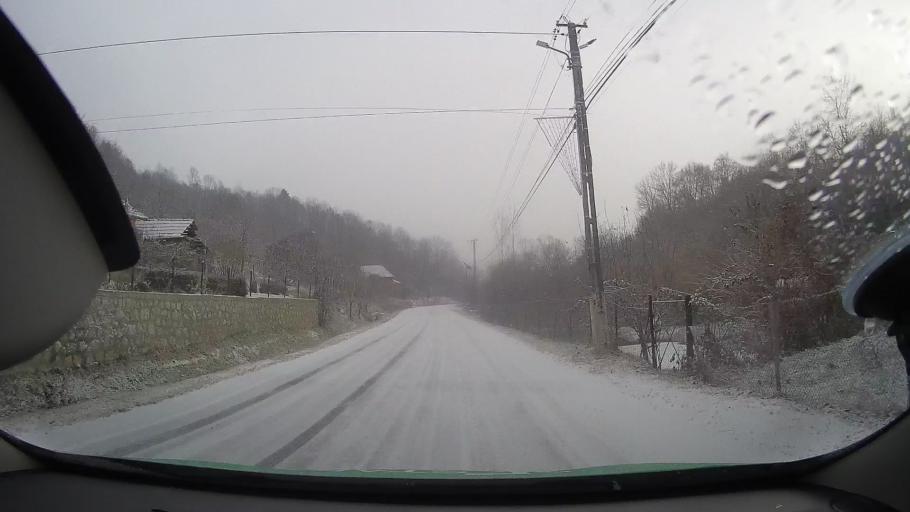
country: RO
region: Alba
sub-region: Comuna Livezile
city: Livezile
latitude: 46.3662
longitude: 23.5954
